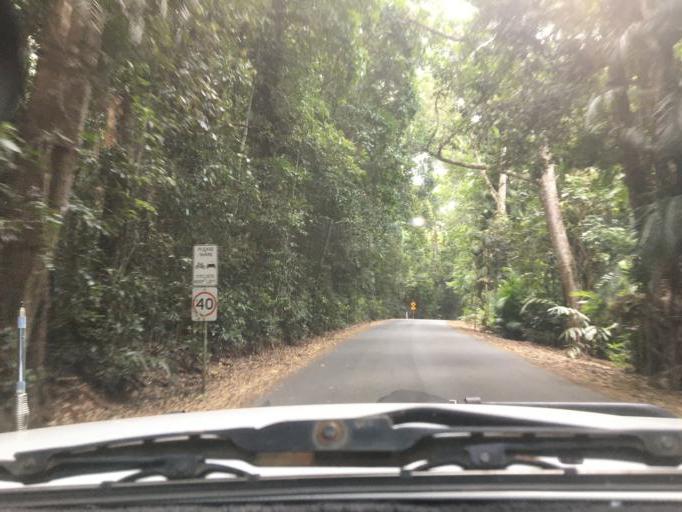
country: AU
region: Queensland
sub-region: Tablelands
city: Tolga
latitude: -17.2823
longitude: 145.6287
